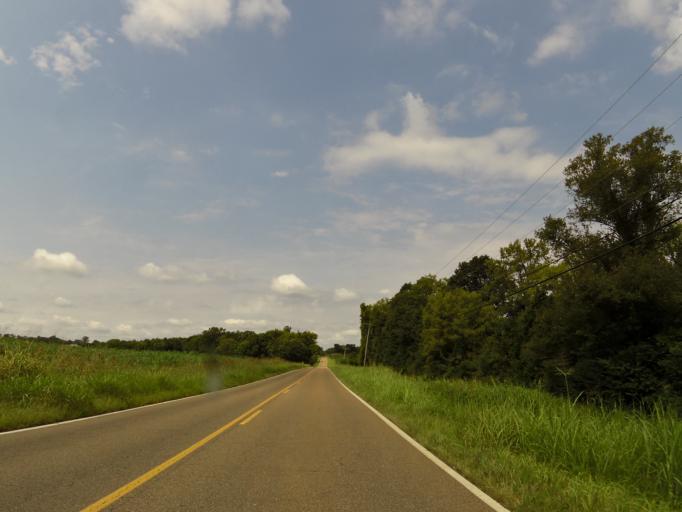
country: US
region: Tennessee
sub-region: Decatur County
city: Decaturville
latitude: 35.5798
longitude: -88.0996
